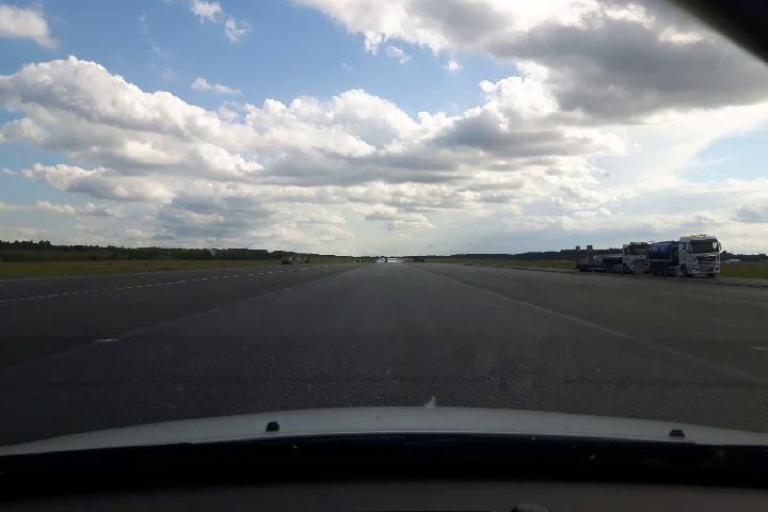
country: SE
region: Stockholm
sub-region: Sigtuna Kommun
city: Rosersberg
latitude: 59.6459
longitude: 17.9577
